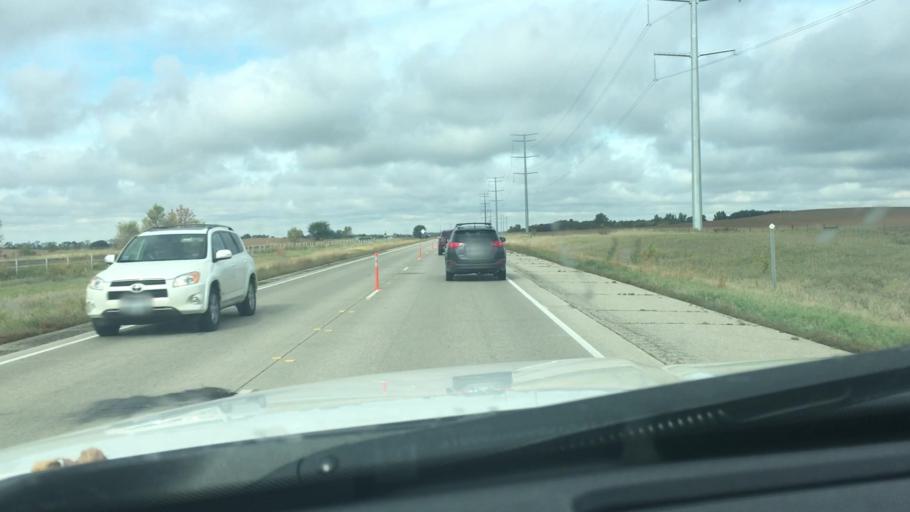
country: US
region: Minnesota
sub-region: Douglas County
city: Alexandria
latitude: 45.9227
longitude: -95.5628
